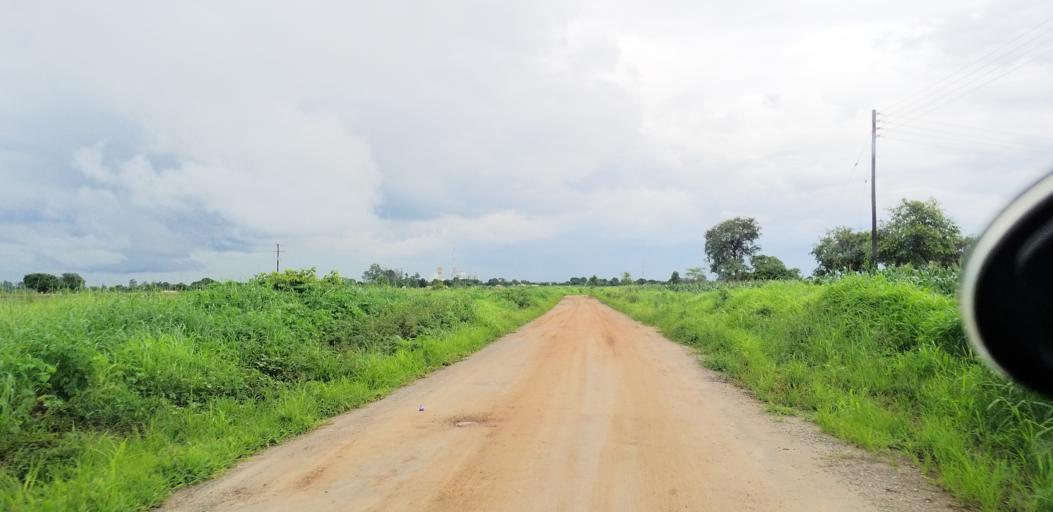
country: ZM
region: Lusaka
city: Lusaka
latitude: -15.5218
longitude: 28.3122
